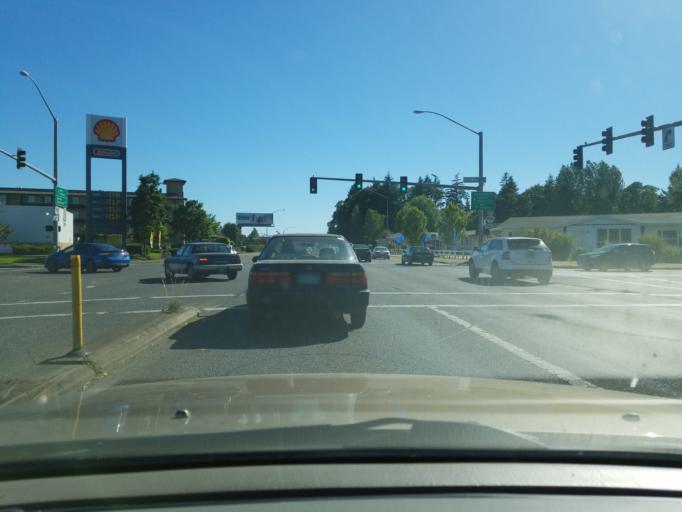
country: US
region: Oregon
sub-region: Yamhill County
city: McMinnville
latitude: 45.1945
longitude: -123.2103
